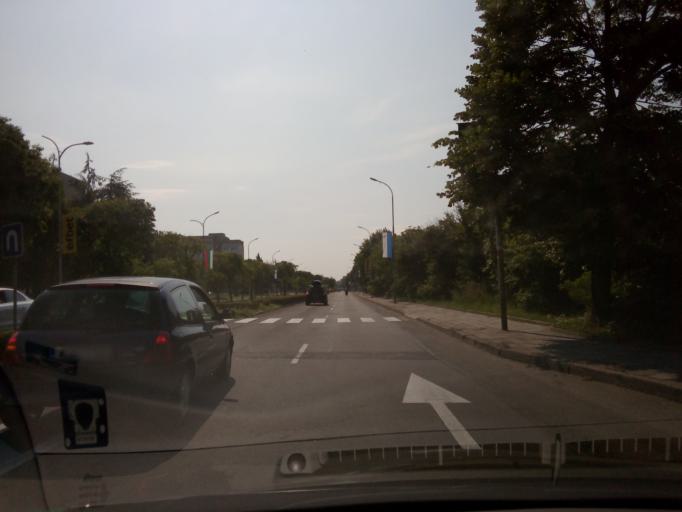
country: BG
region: Burgas
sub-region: Obshtina Pomorie
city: Pomorie
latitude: 42.5631
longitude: 27.6289
